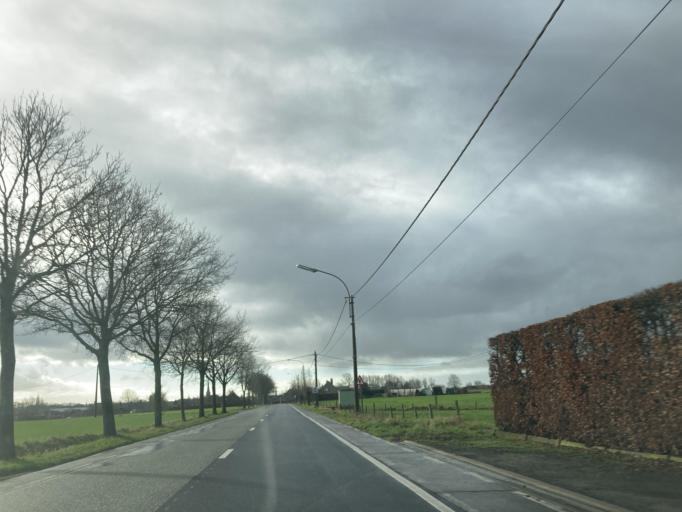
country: BE
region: Flanders
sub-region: Provincie West-Vlaanderen
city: Tielt
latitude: 51.0120
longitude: 3.3286
